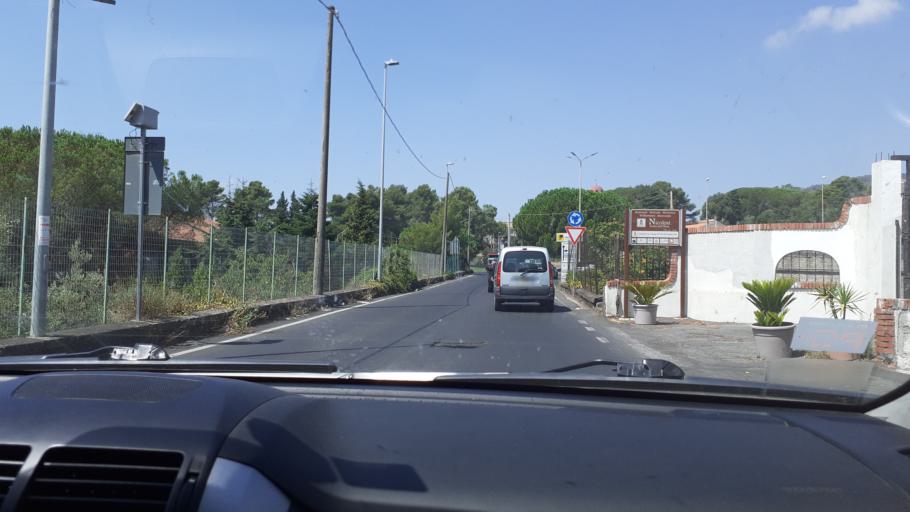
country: IT
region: Sicily
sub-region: Catania
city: Nicolosi
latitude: 37.6146
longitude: 15.0374
